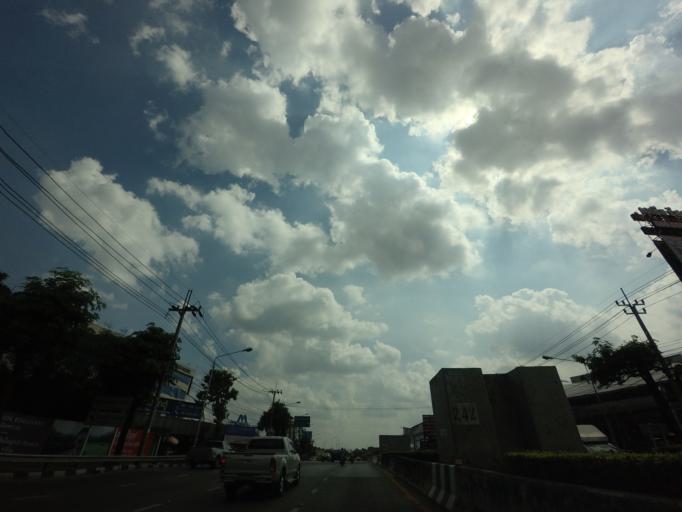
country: TH
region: Bangkok
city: Lat Phrao
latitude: 13.8169
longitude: 100.6400
